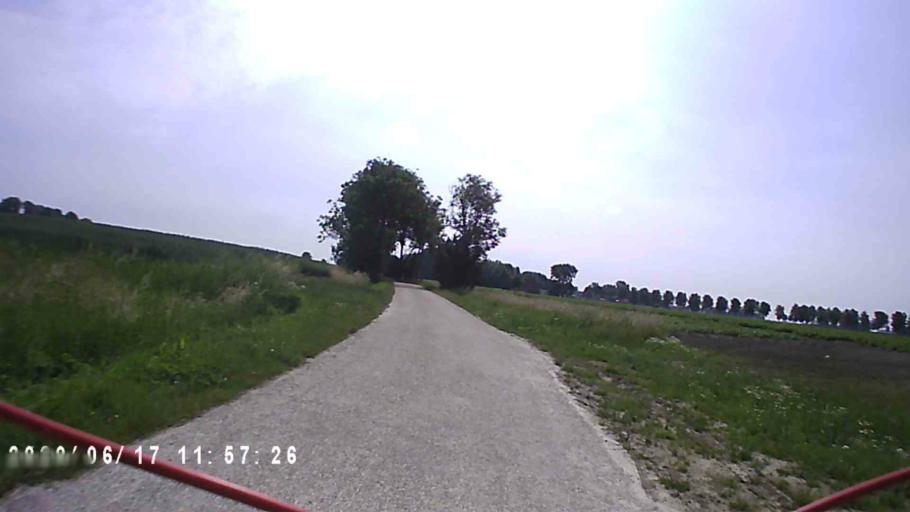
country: NL
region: Groningen
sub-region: Gemeente De Marne
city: Ulrum
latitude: 53.3464
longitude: 6.3241
